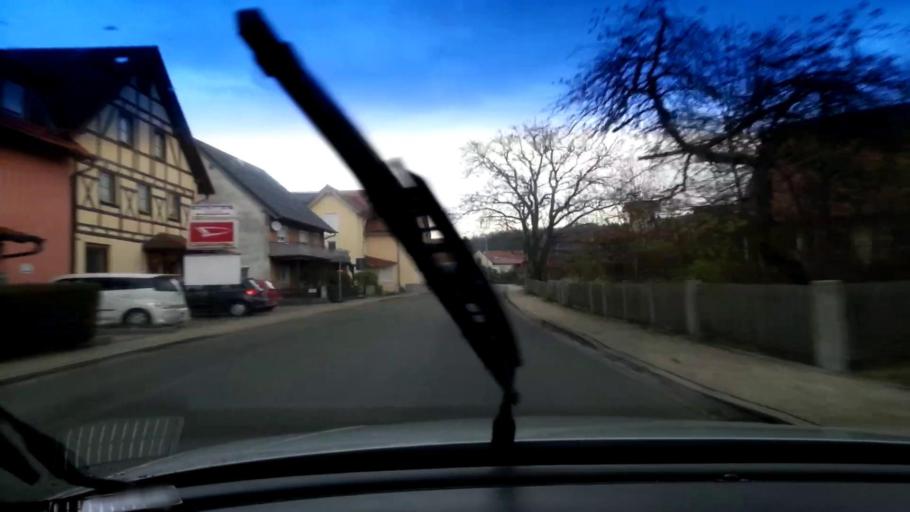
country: DE
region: Bavaria
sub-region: Upper Franconia
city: Litzendorf
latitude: 49.9260
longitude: 11.0063
